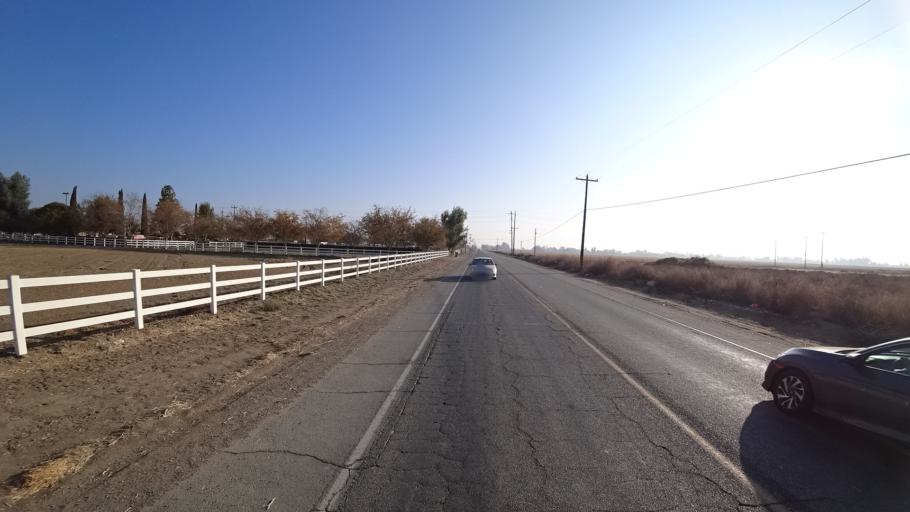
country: US
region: California
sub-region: Kern County
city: Greenfield
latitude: 35.2524
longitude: -118.9778
